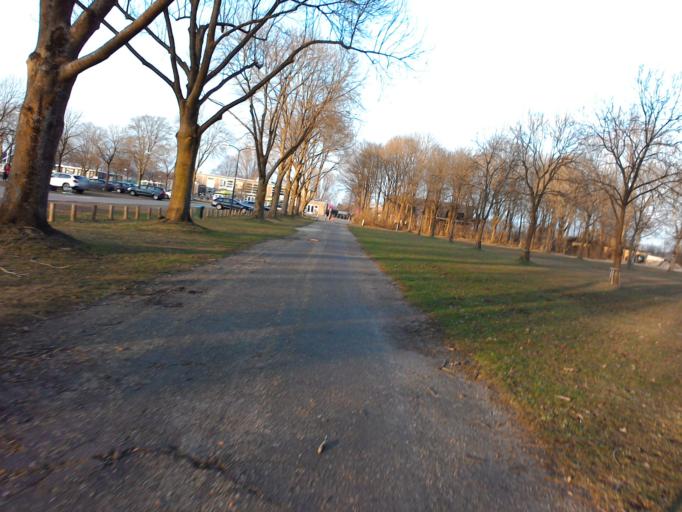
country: NL
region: Utrecht
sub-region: Stichtse Vecht
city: Maarssen
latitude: 52.1413
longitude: 5.0786
